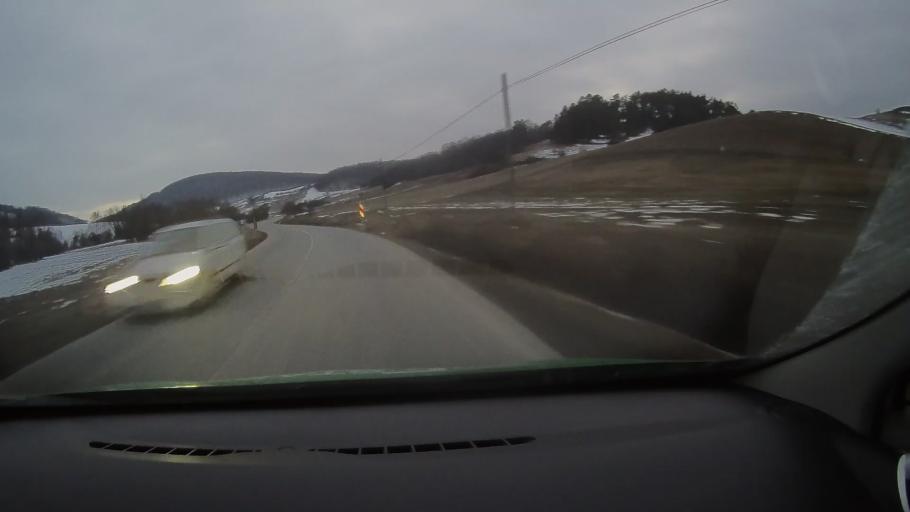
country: RO
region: Harghita
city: Taureni
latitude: 46.2343
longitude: 25.2455
